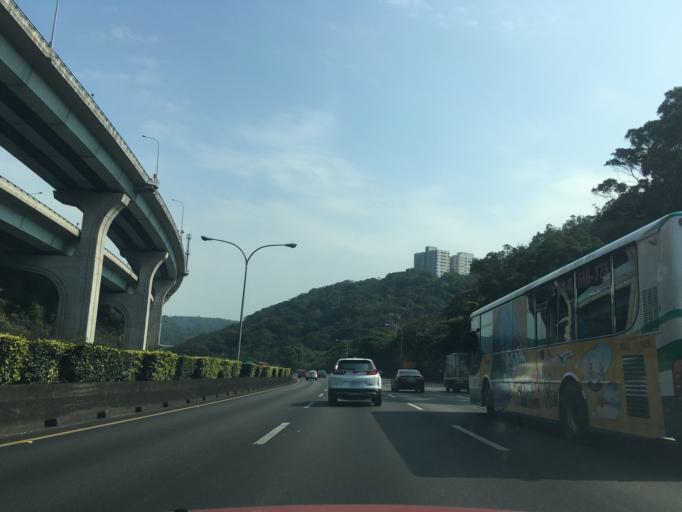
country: TW
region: Taiwan
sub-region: Taoyuan
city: Taoyuan
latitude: 25.0650
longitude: 121.3804
